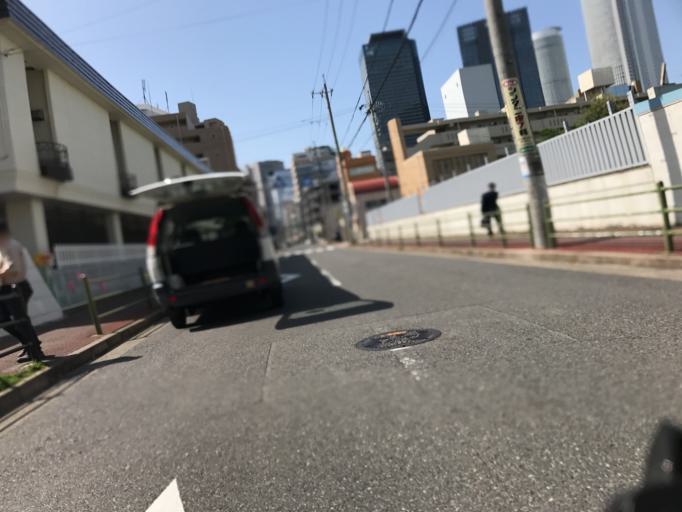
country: JP
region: Aichi
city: Nagoya-shi
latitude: 35.1763
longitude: 136.8870
